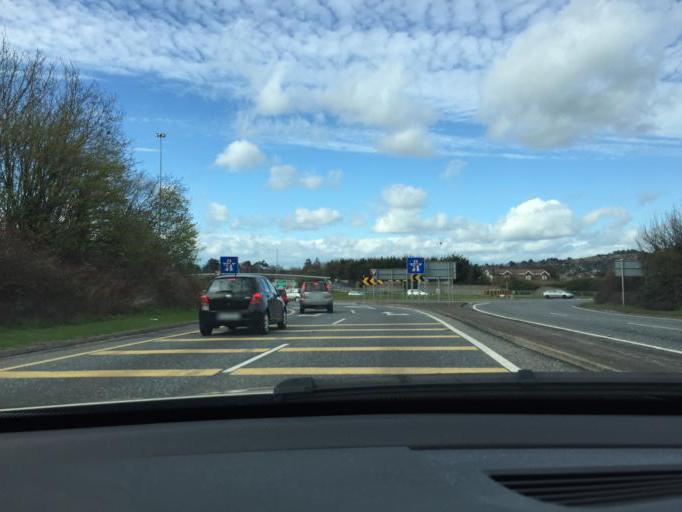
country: IE
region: Leinster
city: Loughlinstown
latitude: 53.2406
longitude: -6.1291
